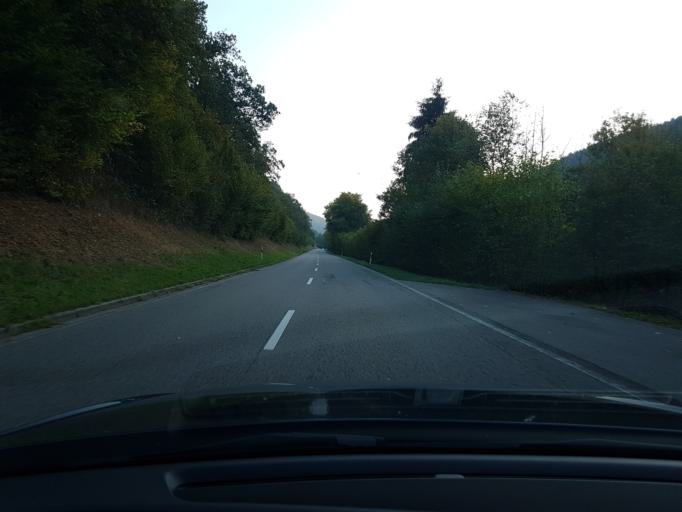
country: DE
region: Baden-Wuerttemberg
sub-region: Karlsruhe Region
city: Eberbach
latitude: 49.4804
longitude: 8.9656
